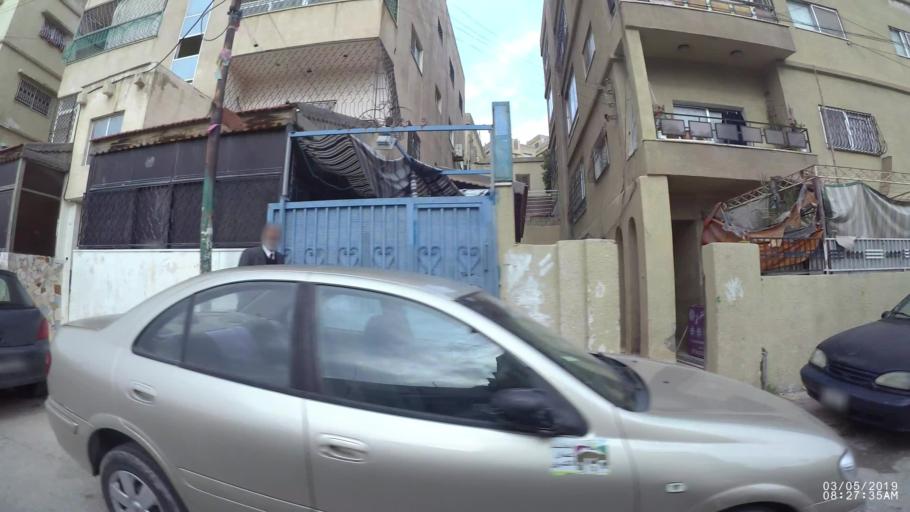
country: JO
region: Amman
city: Amman
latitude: 31.9607
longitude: 35.9337
